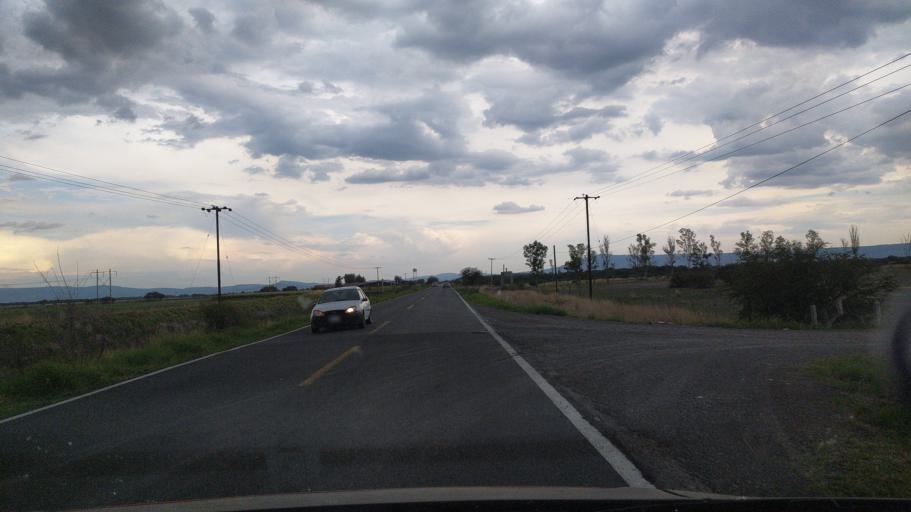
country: MX
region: Guanajuato
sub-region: San Francisco del Rincon
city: San Ignacio de Hidalgo
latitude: 20.8499
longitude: -101.8946
